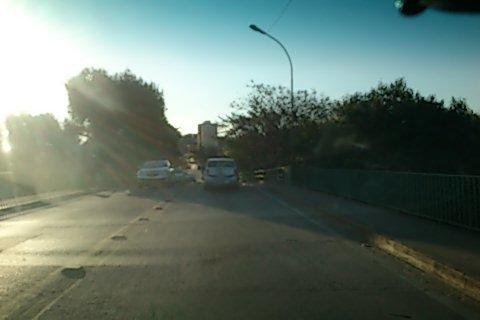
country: BR
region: Sao Paulo
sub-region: Sao Jose Dos Campos
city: Sao Jose dos Campos
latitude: -23.1618
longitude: -45.9035
